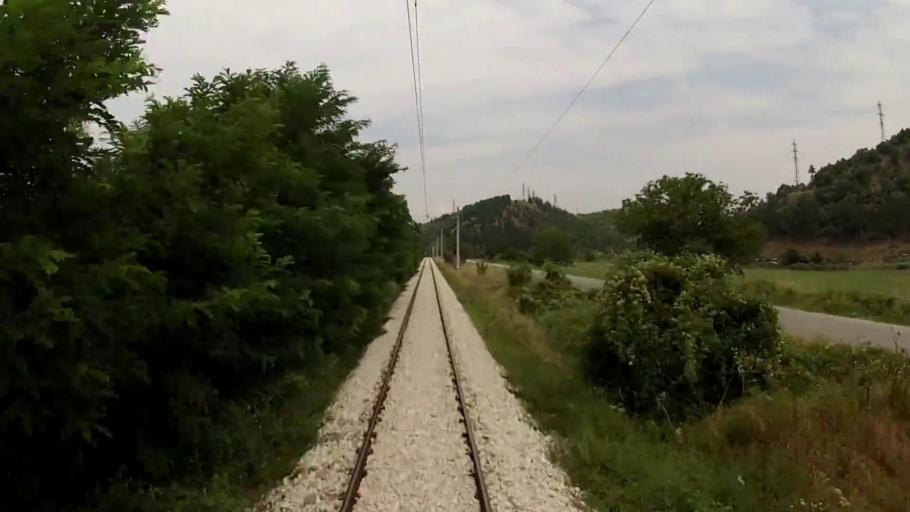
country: BG
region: Blagoevgrad
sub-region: Obshtina Blagoevgrad
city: Blagoevgrad
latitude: 41.9646
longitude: 23.1003
